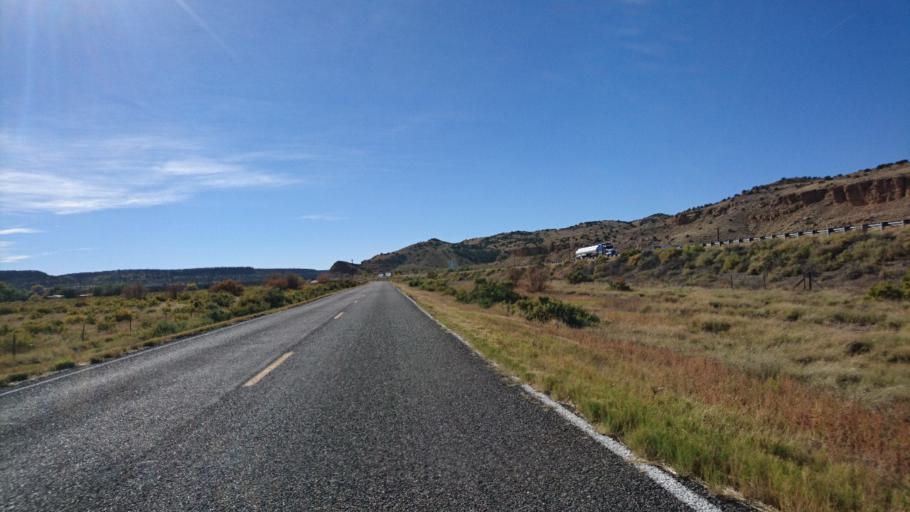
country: US
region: New Mexico
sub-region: Cibola County
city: Skyline-Ganipa
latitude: 35.0701
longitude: -107.6755
